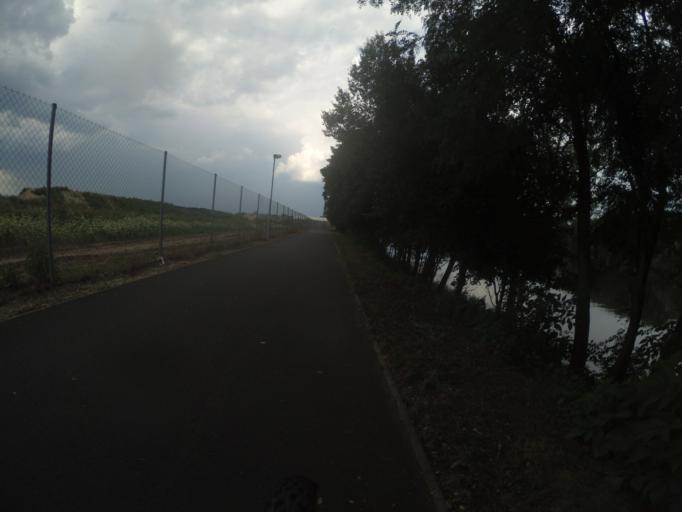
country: CZ
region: Central Bohemia
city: Dolni Berkovice
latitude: 50.3801
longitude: 14.4510
